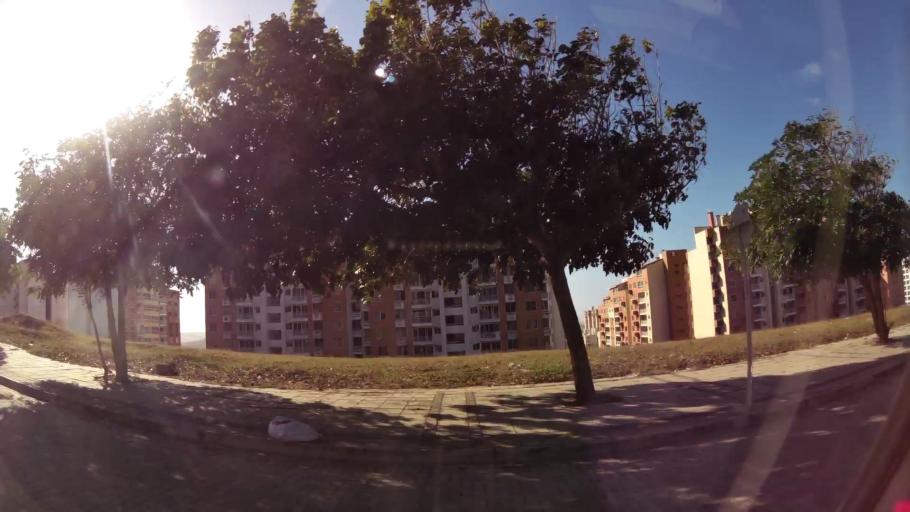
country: CO
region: Atlantico
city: Barranquilla
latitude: 11.0056
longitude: -74.8330
